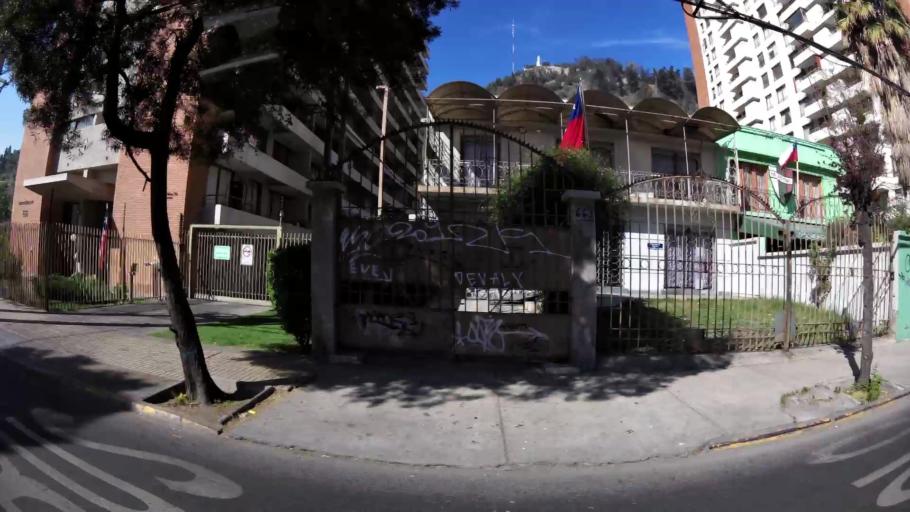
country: CL
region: Santiago Metropolitan
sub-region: Provincia de Santiago
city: Santiago
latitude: -33.4254
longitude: -70.6397
